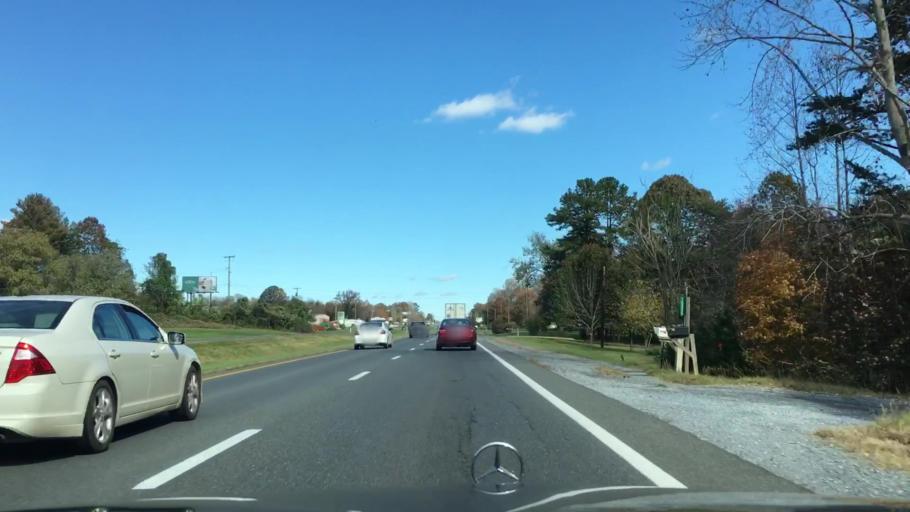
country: US
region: Virginia
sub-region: Campbell County
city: Rustburg
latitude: 37.2690
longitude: -79.1757
